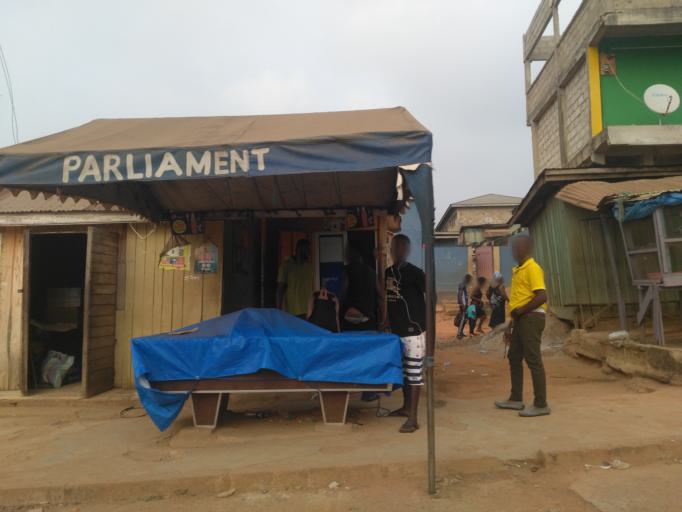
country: GH
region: Ashanti
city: Kumasi
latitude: 6.6798
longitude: -1.5911
